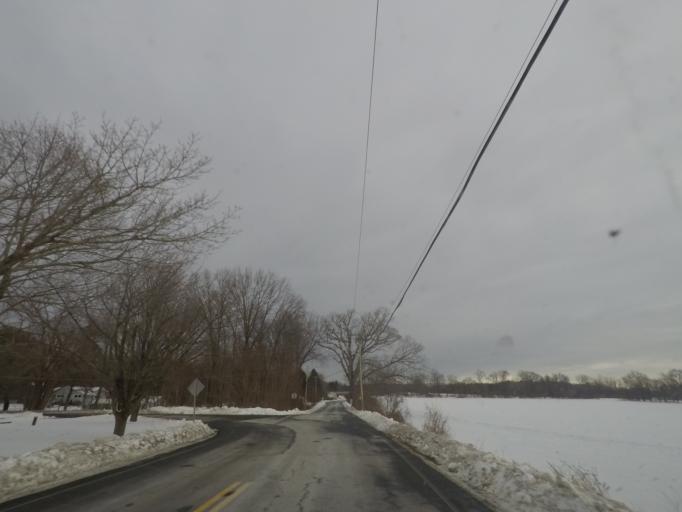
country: US
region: New York
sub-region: Rensselaer County
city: Castleton-on-Hudson
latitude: 42.5136
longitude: -73.6937
